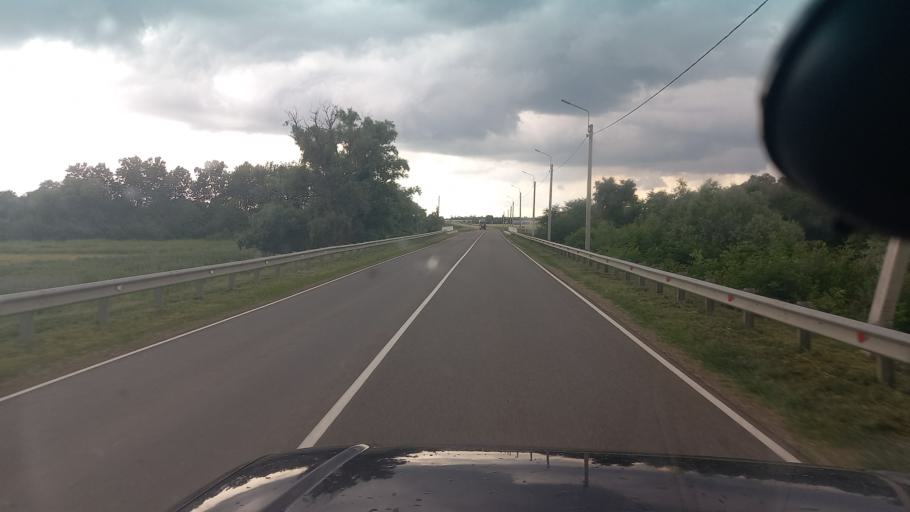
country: RU
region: Adygeya
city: Shovgenovskiy
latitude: 44.9991
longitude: 40.1484
